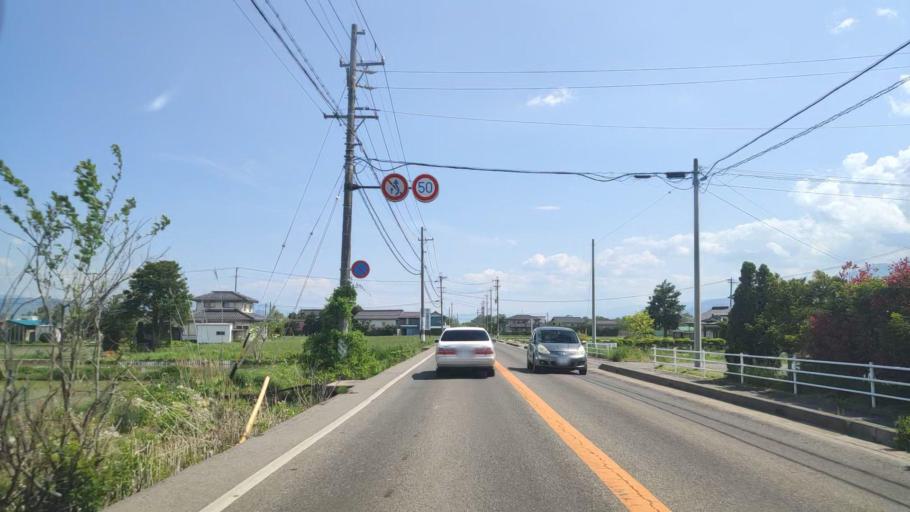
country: JP
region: Nagano
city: Hotaka
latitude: 36.3897
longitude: 137.8645
